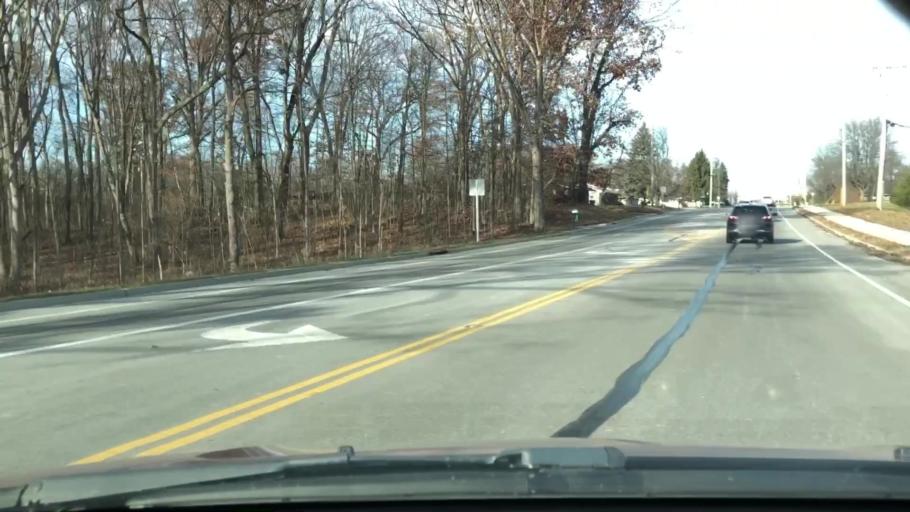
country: US
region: Ohio
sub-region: Greene County
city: Wright-Patterson AFB
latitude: 39.7651
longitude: -84.0759
